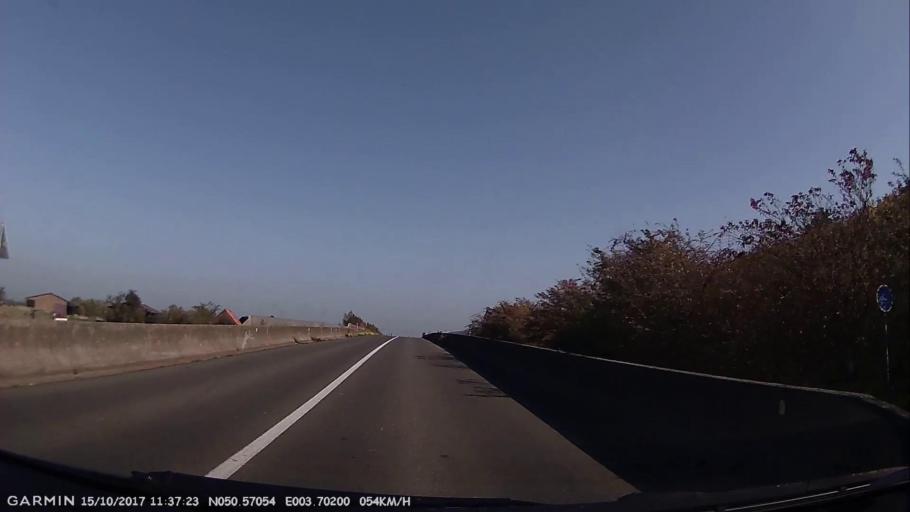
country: BE
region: Wallonia
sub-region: Province du Hainaut
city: Beloeil
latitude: 50.5707
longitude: 3.7022
